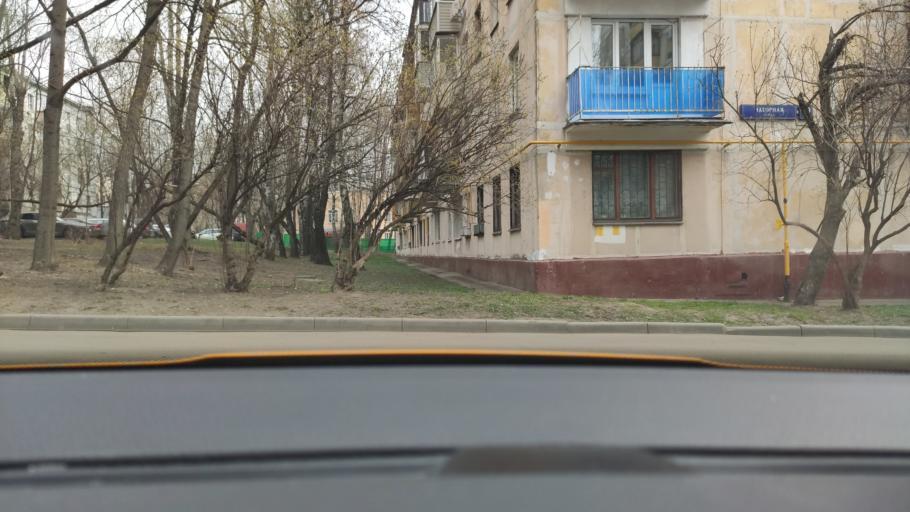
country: RU
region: Moscow
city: Kotlovka
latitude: 55.6687
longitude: 37.5938
